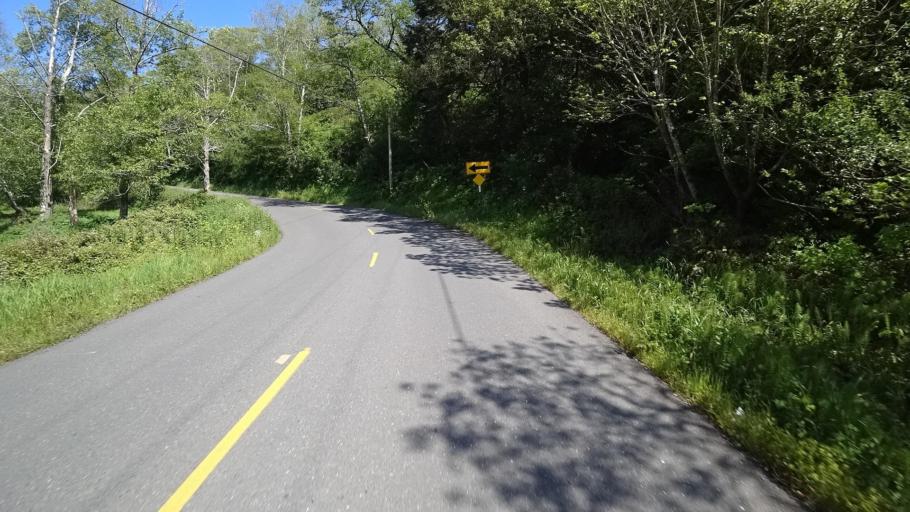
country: US
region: California
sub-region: Humboldt County
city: Fortuna
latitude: 40.5630
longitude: -124.1428
